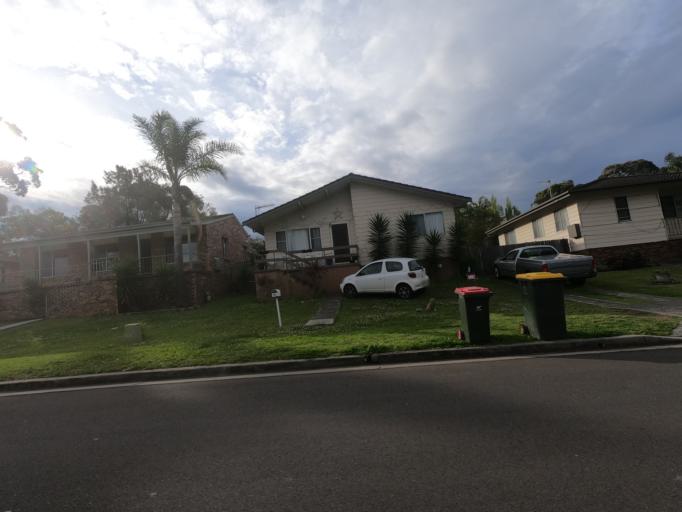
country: AU
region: New South Wales
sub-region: Wollongong
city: Berkeley
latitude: -34.4772
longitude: 150.8479
